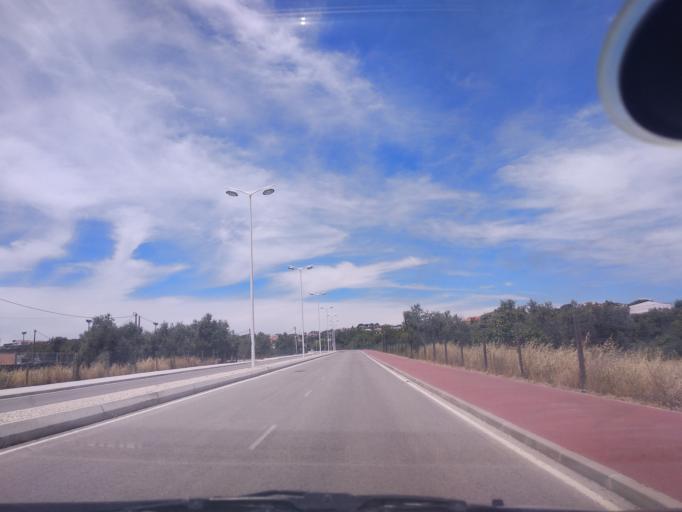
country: PT
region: Faro
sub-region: Sao Bras de Alportel
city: Sao Bras de Alportel
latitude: 37.1558
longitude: -7.8778
